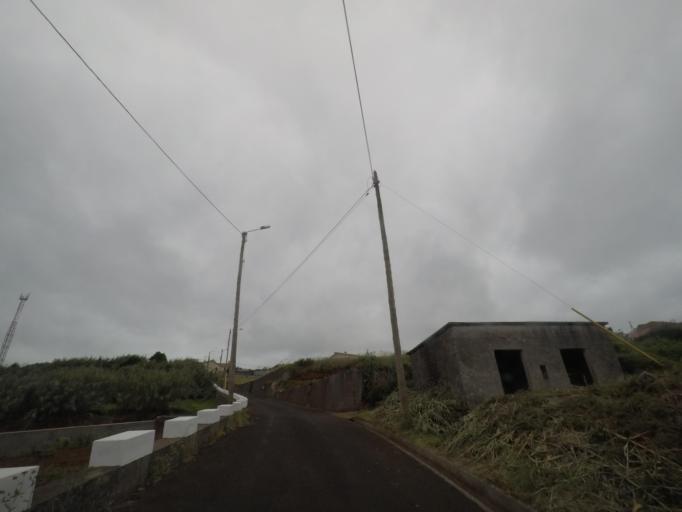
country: PT
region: Madeira
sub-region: Porto Moniz
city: Porto Moniz
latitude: 32.8596
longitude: -17.1788
